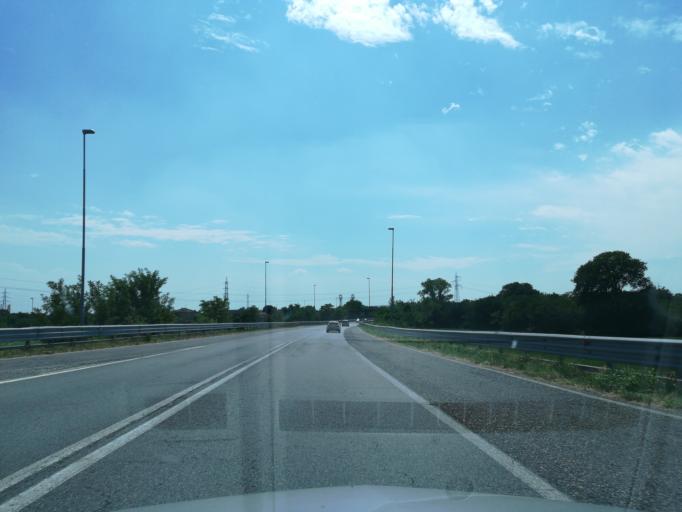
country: IT
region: Lombardy
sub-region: Provincia di Bergamo
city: Grassobbio
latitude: 45.6442
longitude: 9.7292
